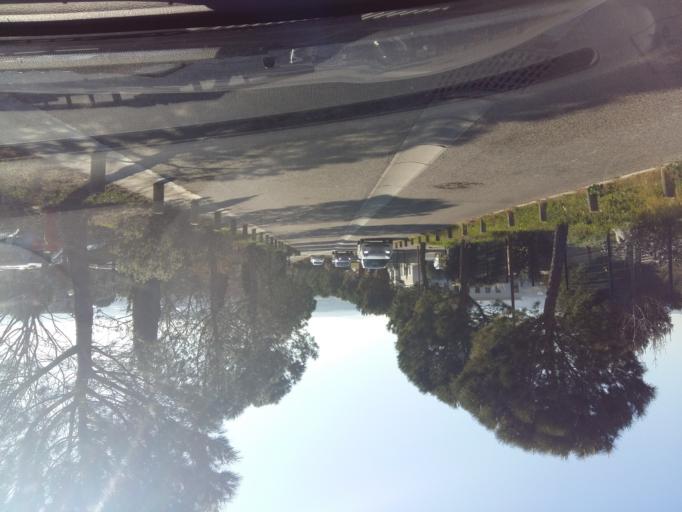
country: FR
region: Provence-Alpes-Cote d'Azur
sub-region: Departement des Bouches-du-Rhone
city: Ventabren
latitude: 43.4966
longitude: 5.3449
